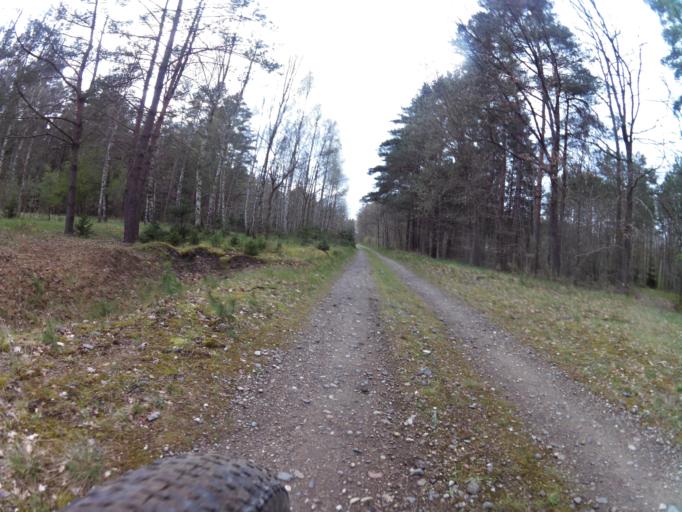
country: PL
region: West Pomeranian Voivodeship
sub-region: Powiat slawienski
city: Slawno
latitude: 54.3236
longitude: 16.7622
